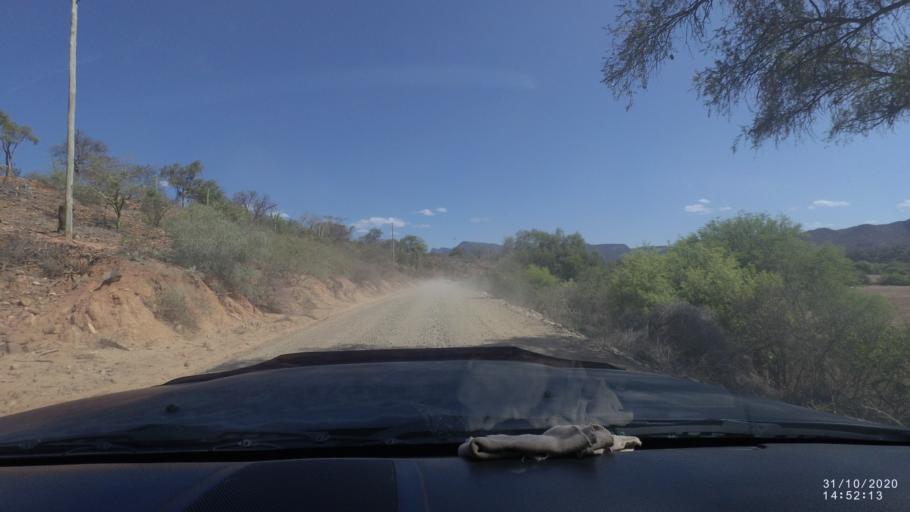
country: BO
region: Cochabamba
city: Aiquile
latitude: -18.2120
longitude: -64.8565
